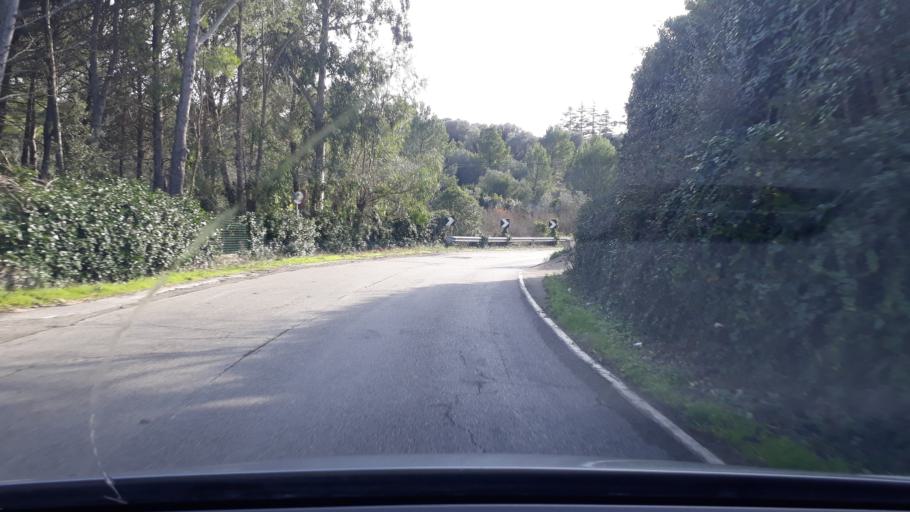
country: IT
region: Apulia
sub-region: Provincia di Taranto
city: Martina Franca
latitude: 40.6888
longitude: 17.3507
